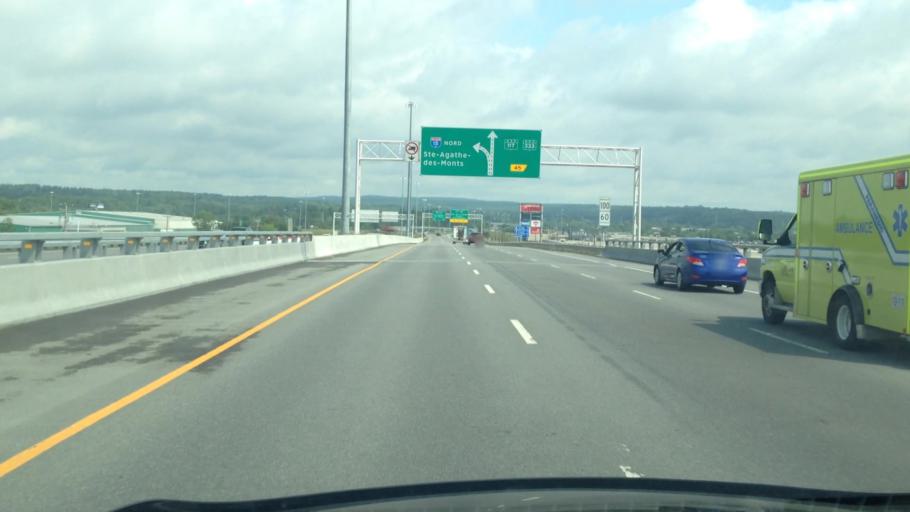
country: CA
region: Quebec
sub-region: Laurentides
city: Saint-Jerome
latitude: 45.7876
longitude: -74.0203
